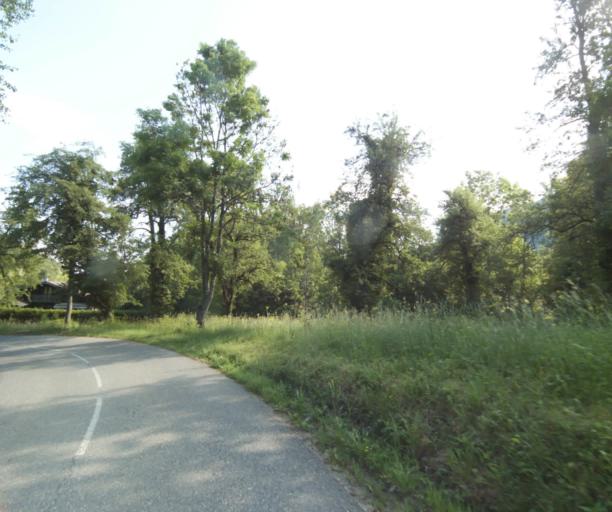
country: FR
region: Rhone-Alpes
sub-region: Departement de la Haute-Savoie
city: Lyaud
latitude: 46.3086
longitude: 6.5019
